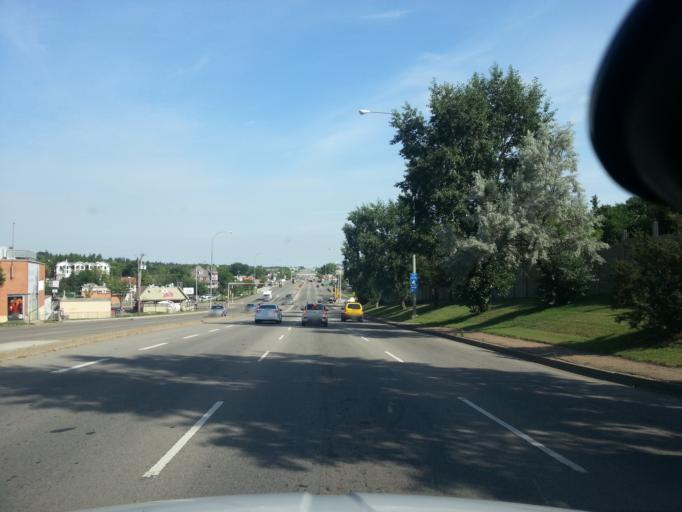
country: CA
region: Alberta
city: St. Albert
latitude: 53.6342
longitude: -113.6229
